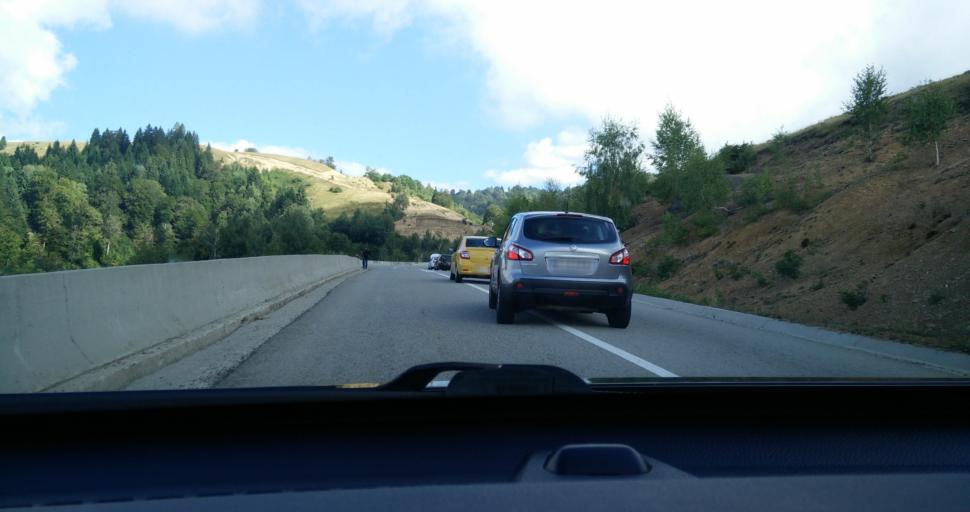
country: RO
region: Gorj
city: Novaci-Straini
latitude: 45.2214
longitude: 23.6959
